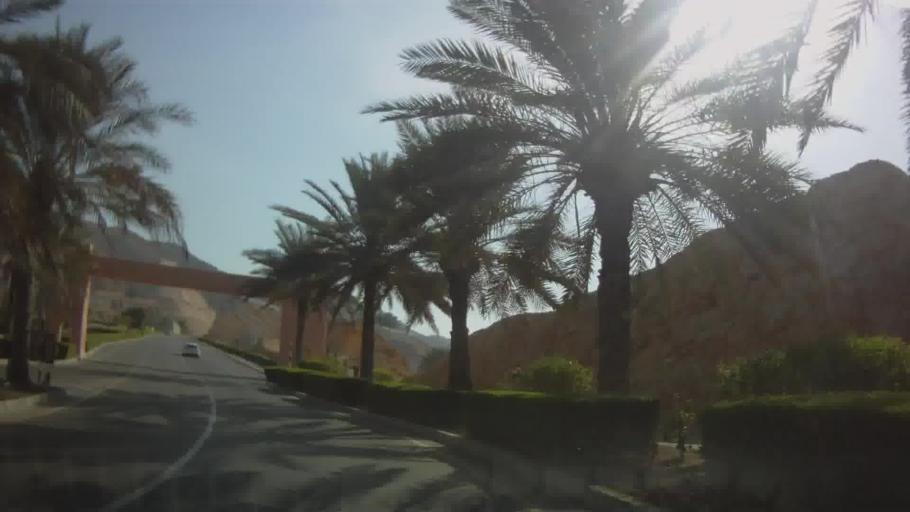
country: OM
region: Muhafazat Masqat
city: Muscat
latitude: 23.5499
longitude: 58.6580
